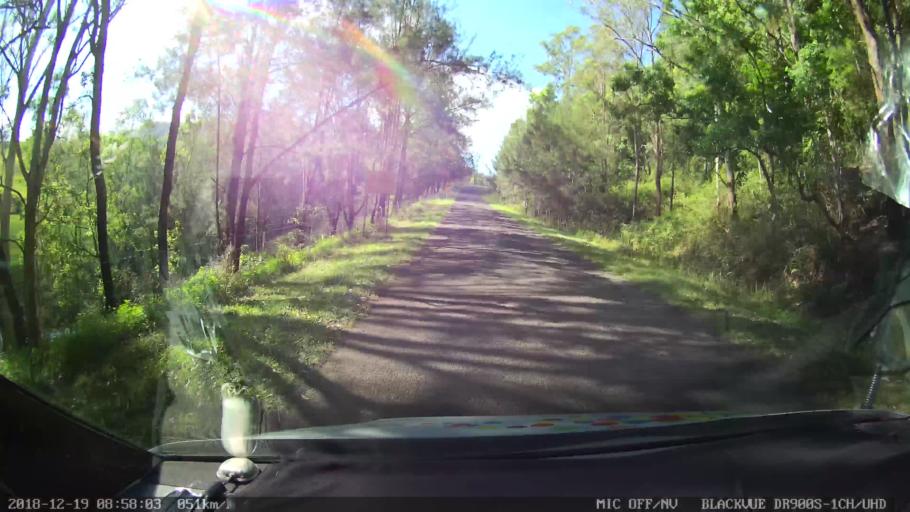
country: AU
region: New South Wales
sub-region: Kyogle
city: Kyogle
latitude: -28.4226
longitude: 152.9677
